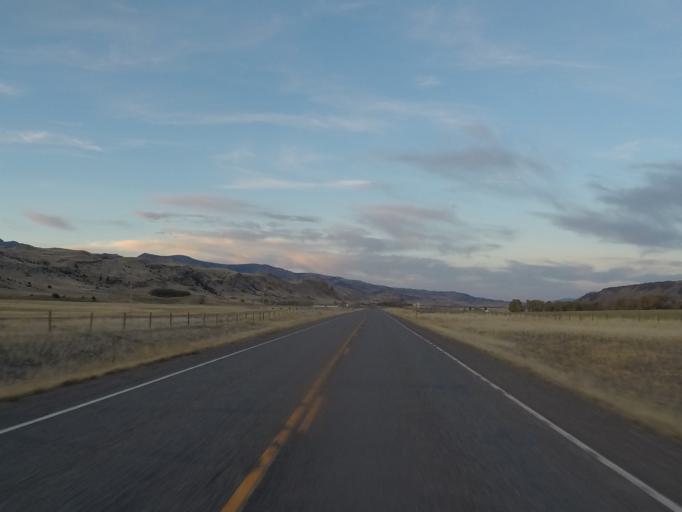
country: US
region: Montana
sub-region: Gallatin County
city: Bozeman
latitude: 45.2657
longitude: -110.8630
